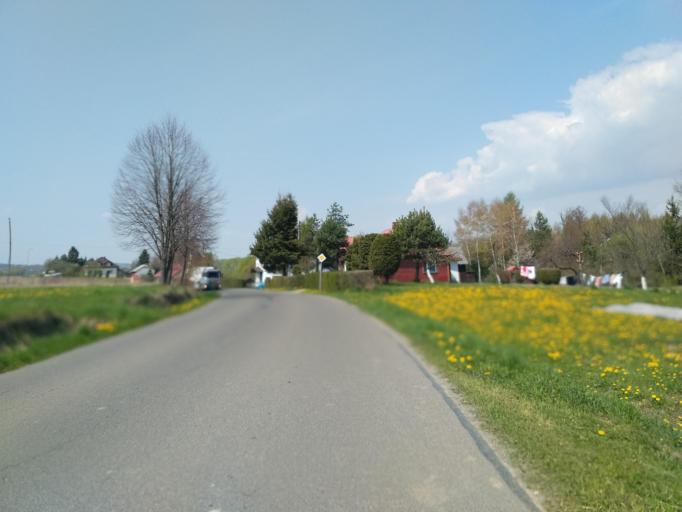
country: PL
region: Subcarpathian Voivodeship
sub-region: Powiat krosnienski
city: Chorkowka
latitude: 49.6634
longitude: 21.6345
